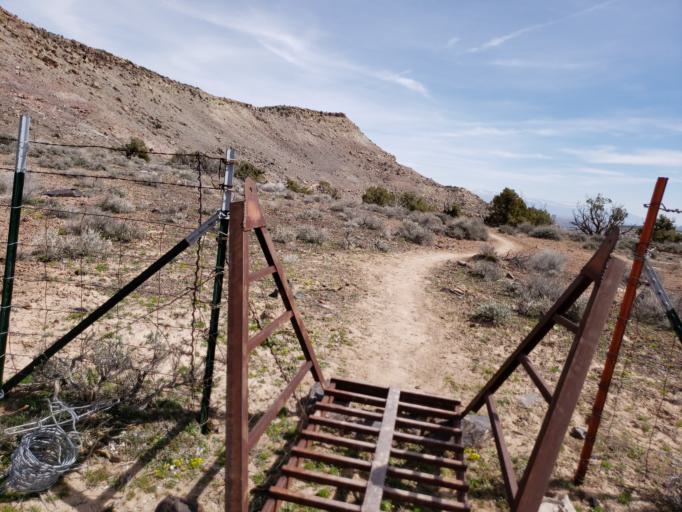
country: US
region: Colorado
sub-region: Mesa County
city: Loma
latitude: 39.1839
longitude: -108.8604
